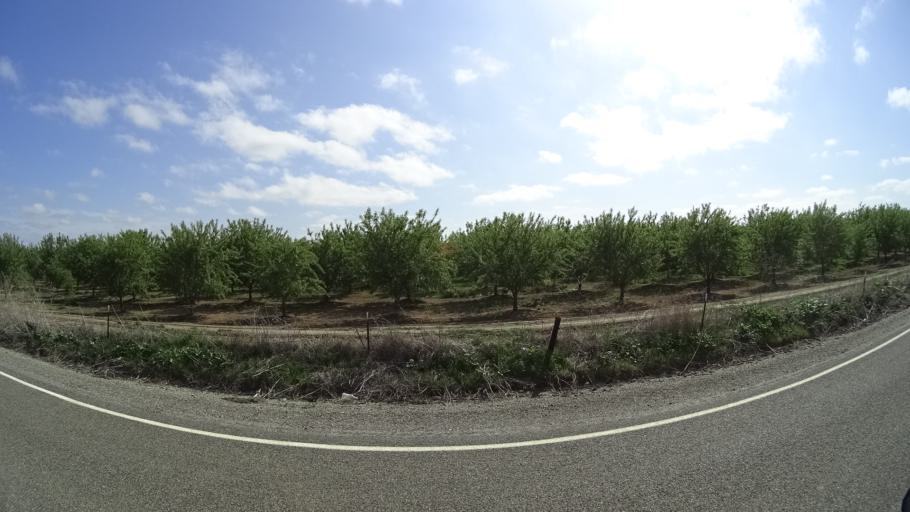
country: US
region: California
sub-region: Colusa County
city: Colusa
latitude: 39.4121
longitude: -121.9294
